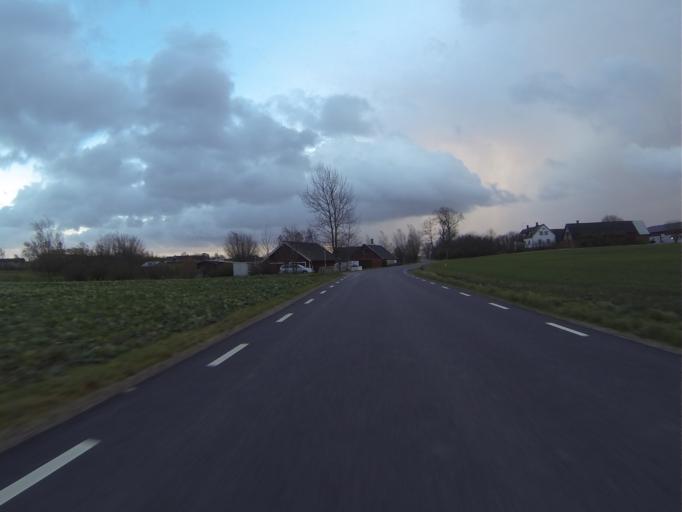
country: SE
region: Skane
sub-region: Lunds Kommun
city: Genarp
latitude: 55.6283
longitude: 13.3314
